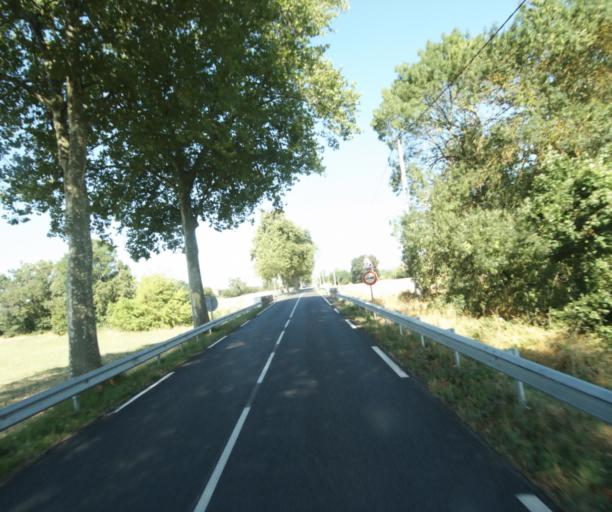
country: FR
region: Midi-Pyrenees
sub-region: Departement de la Haute-Garonne
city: Revel
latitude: 43.4714
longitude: 1.9528
